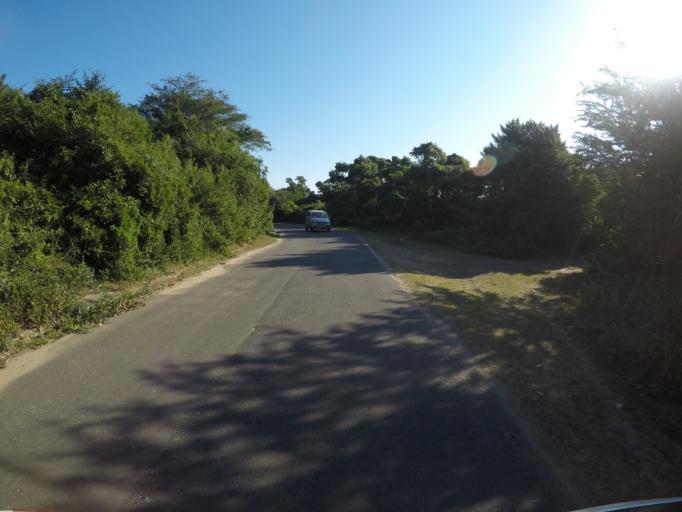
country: ZA
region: KwaZulu-Natal
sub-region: uThungulu District Municipality
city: Richards Bay
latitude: -28.7996
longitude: 32.0790
